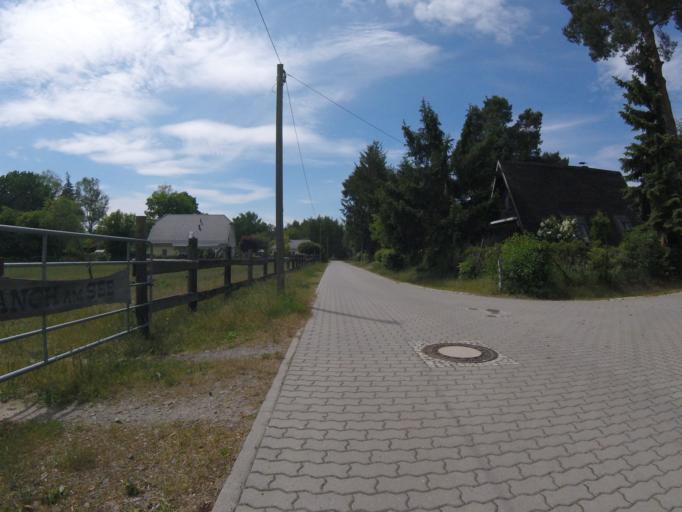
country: DE
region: Brandenburg
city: Bestensee
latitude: 52.2258
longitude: 13.6409
